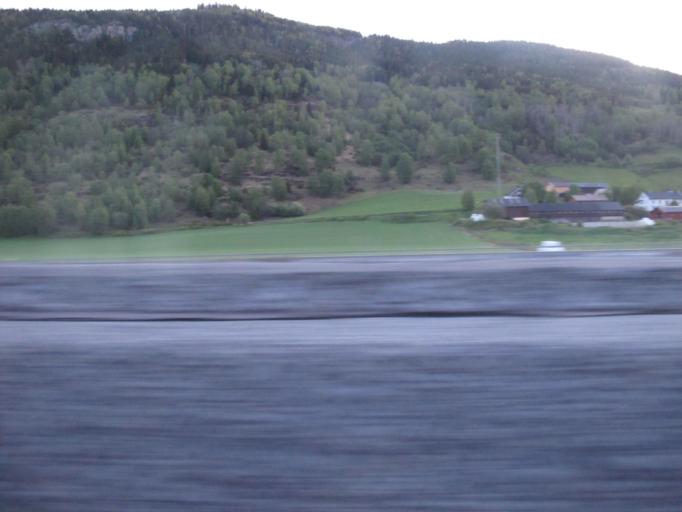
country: NO
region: Oppland
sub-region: Sor-Fron
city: Hundorp
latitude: 61.5478
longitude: 10.0281
